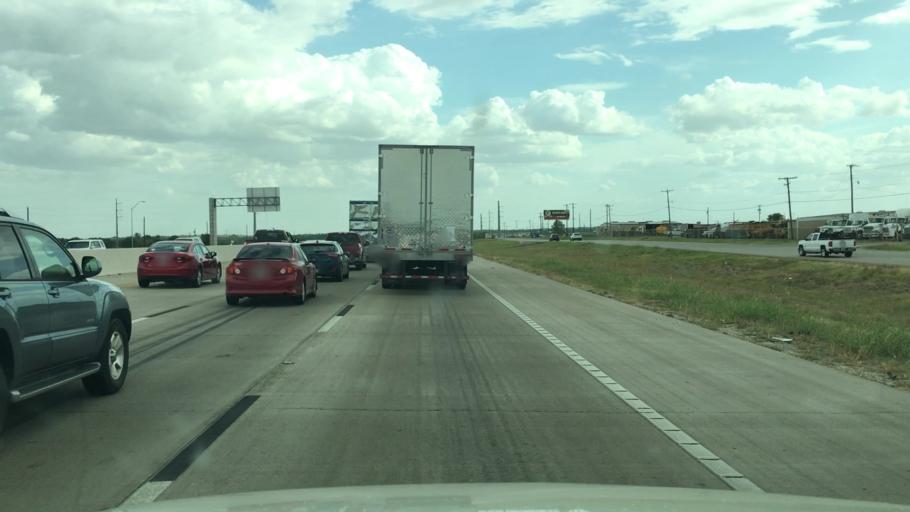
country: US
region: Texas
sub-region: McLennan County
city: Lorena
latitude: 31.3536
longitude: -97.2194
